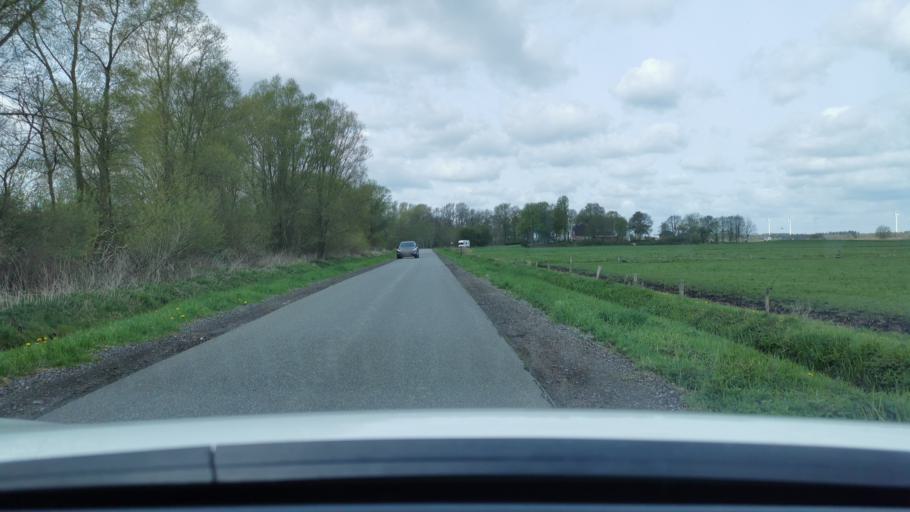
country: DE
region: Schleswig-Holstein
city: Oldenbuttel
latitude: 54.1821
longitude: 9.4465
